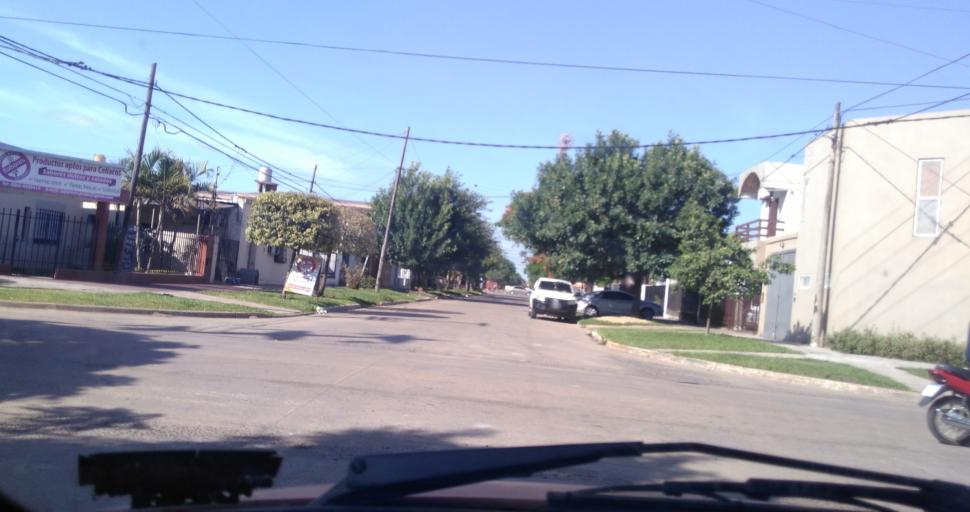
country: AR
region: Chaco
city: Resistencia
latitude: -27.4686
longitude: -58.9648
